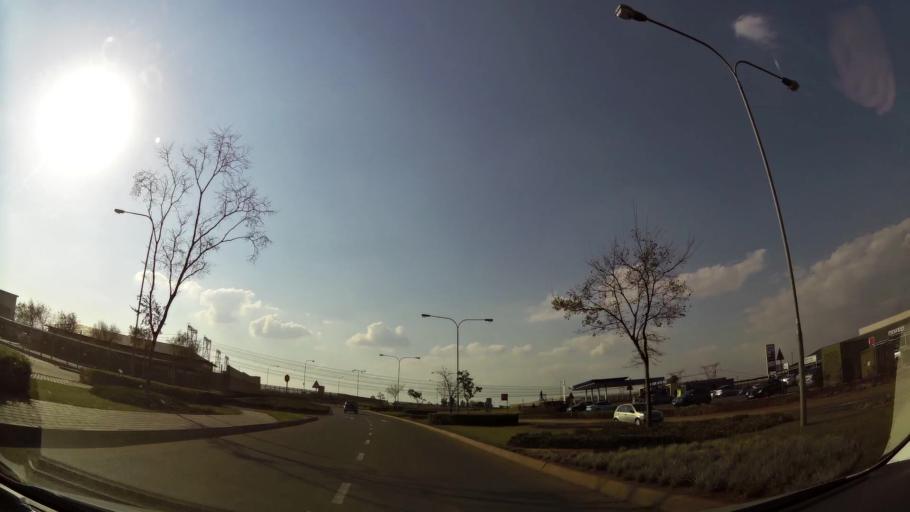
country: ZA
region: Gauteng
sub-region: City of Tshwane Metropolitan Municipality
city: Centurion
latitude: -25.9194
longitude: 28.2100
